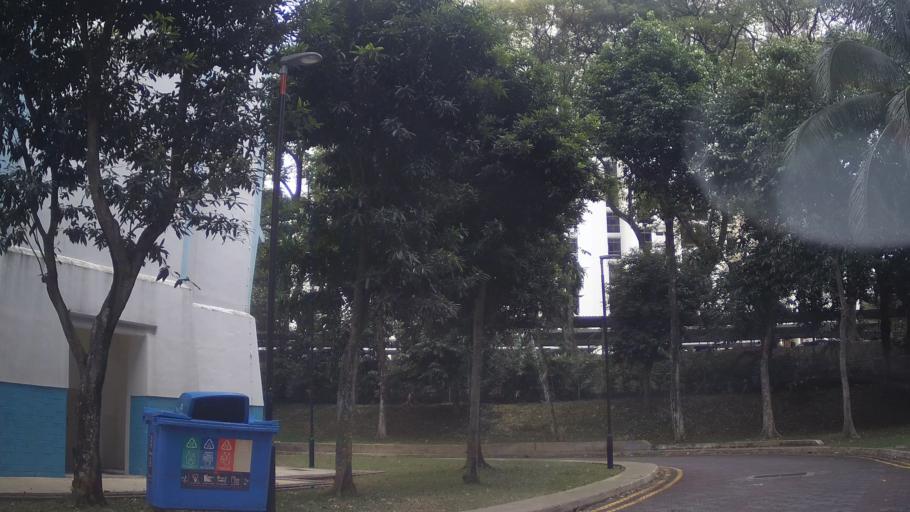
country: MY
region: Johor
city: Johor Bahru
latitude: 1.3752
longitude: 103.7655
